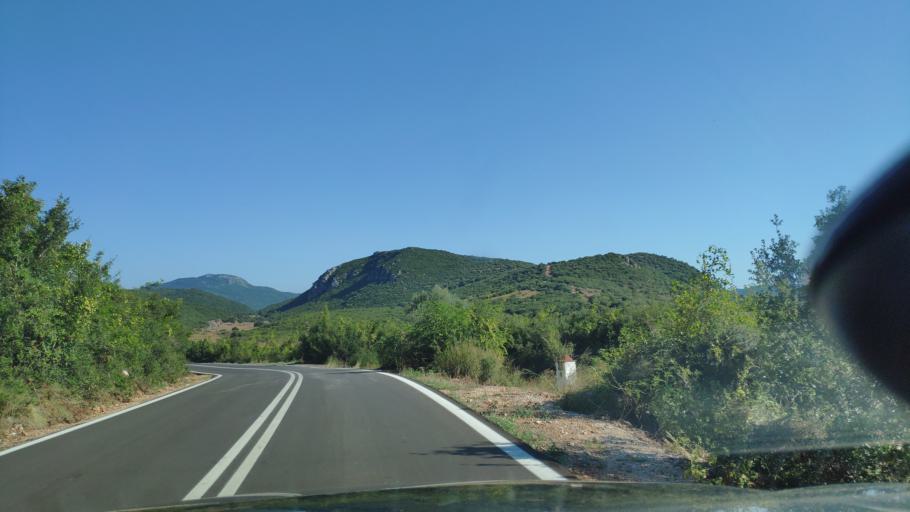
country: GR
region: West Greece
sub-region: Nomos Aitolias kai Akarnanias
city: Fitiai
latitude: 38.6667
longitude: 21.1435
